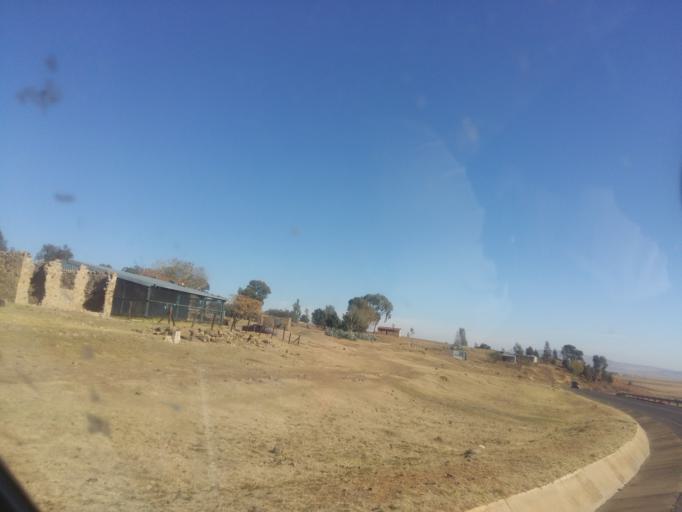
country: LS
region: Mafeteng
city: Mafeteng
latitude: -29.6819
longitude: 27.2813
